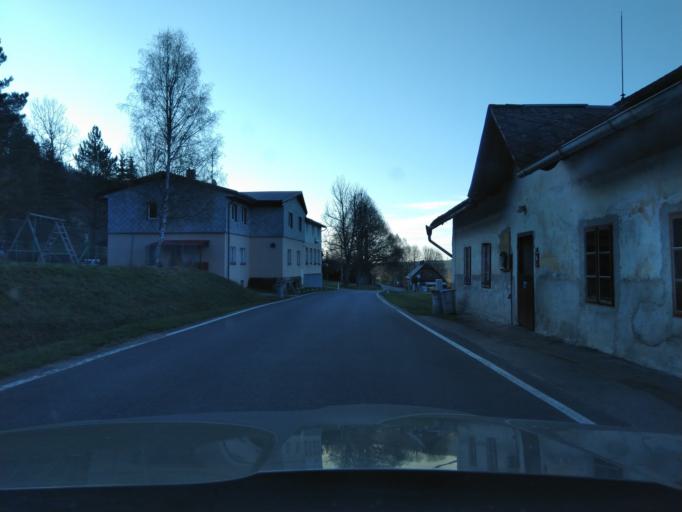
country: CZ
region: Jihocesky
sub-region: Okres Prachatice
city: Volary
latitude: 48.9491
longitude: 13.7863
